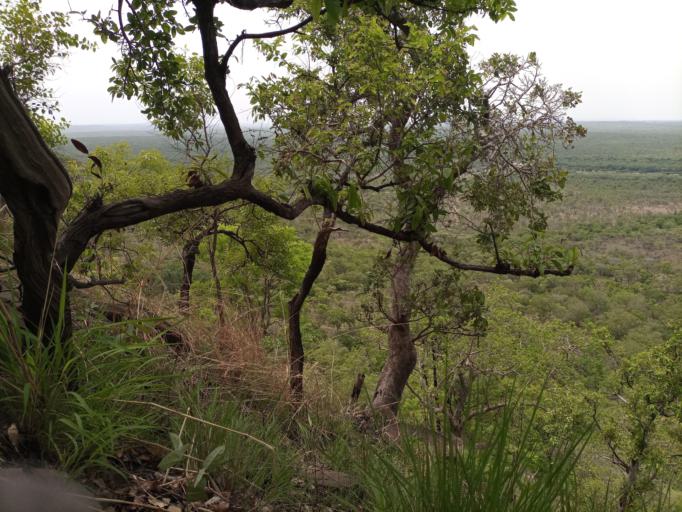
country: GH
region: Upper East
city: Bolgatanga
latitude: 10.5816
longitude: -0.4515
